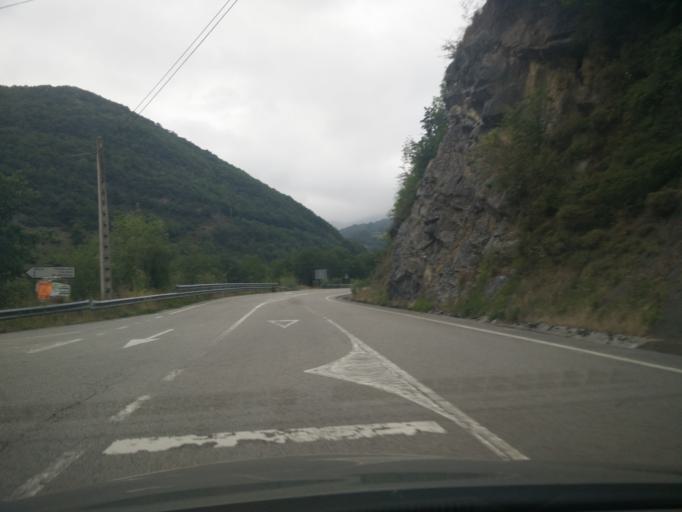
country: ES
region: Asturias
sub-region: Province of Asturias
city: Campo de Caso
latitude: 43.1924
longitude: -5.3820
